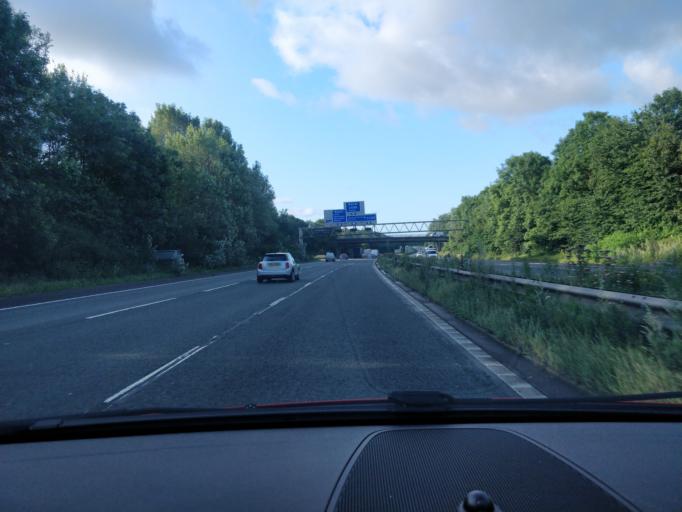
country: GB
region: England
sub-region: Knowsley
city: Prescot
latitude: 53.4154
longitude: -2.8130
